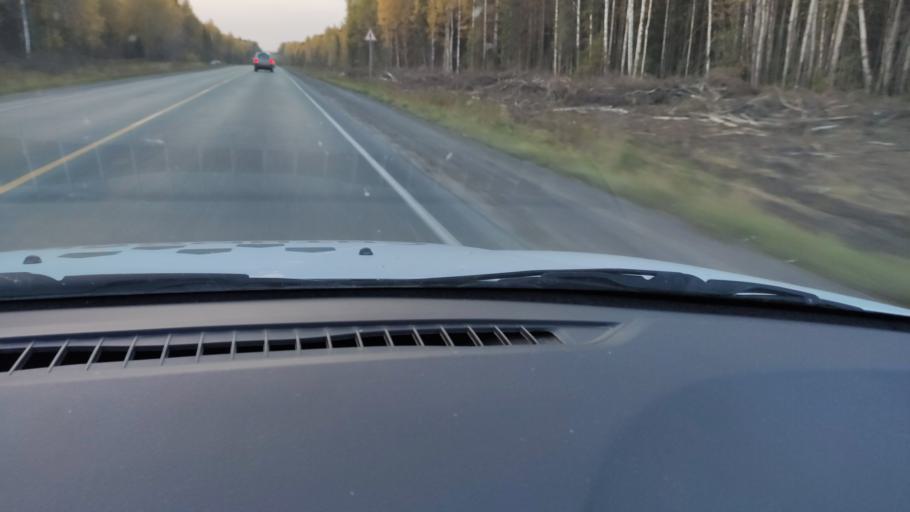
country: RU
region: Perm
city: Kukushtan
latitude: 57.5550
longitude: 56.5780
